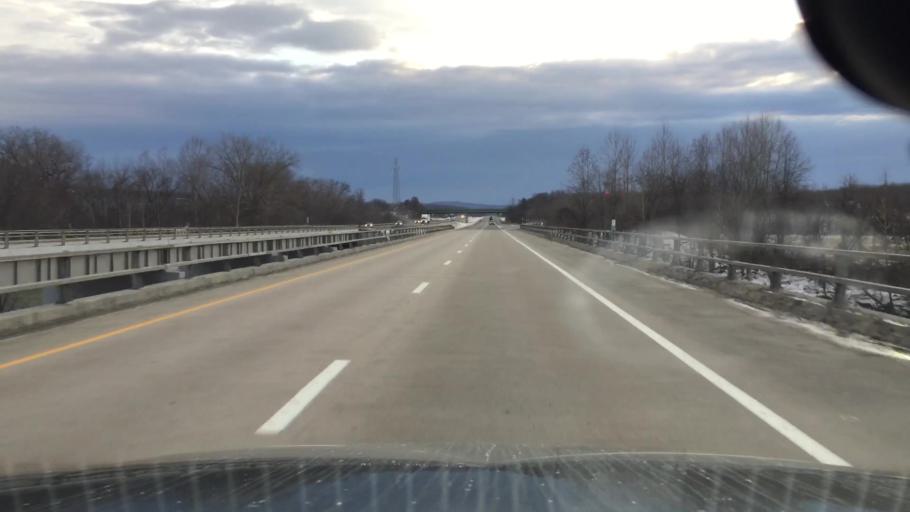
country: US
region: Pennsylvania
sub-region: Bradford County
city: South Waverly
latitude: 42.0008
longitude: -76.5947
